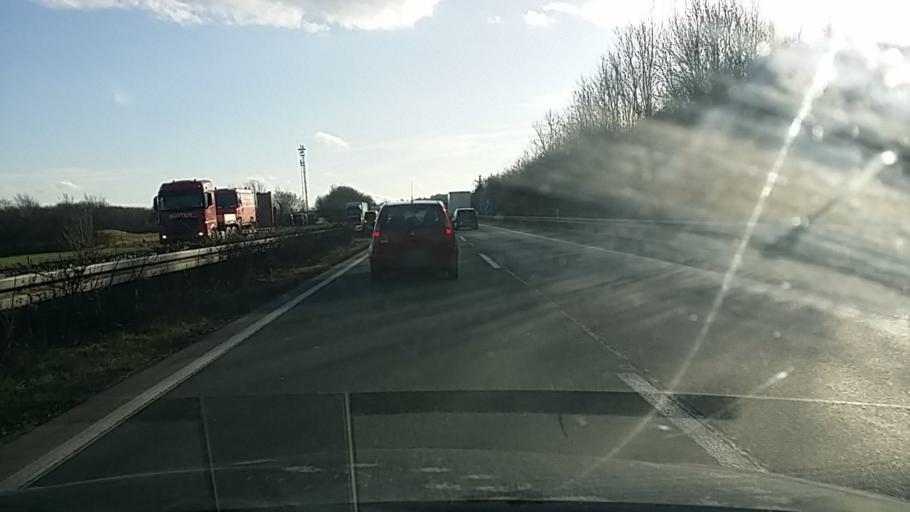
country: DE
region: North Rhine-Westphalia
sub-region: Regierungsbezirk Detmold
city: Paderborn
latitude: 51.6316
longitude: 8.7228
